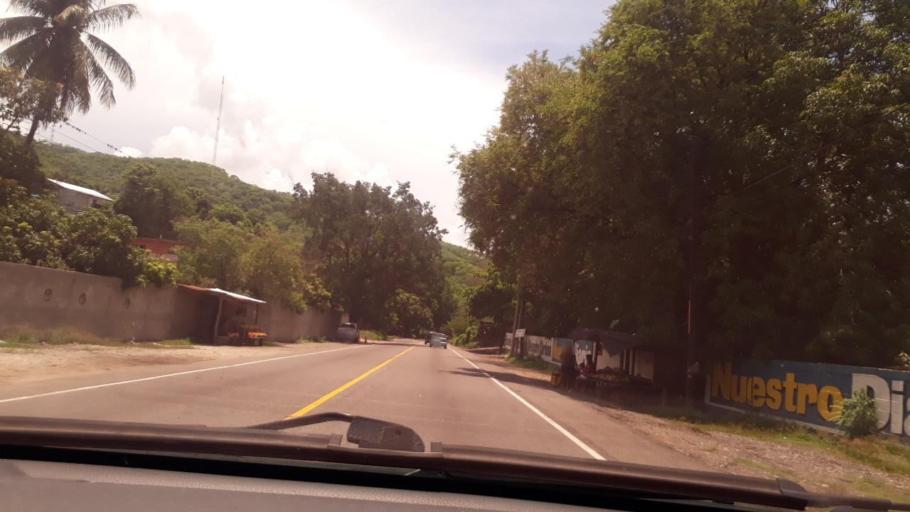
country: GT
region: Zacapa
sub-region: Municipio de Zacapa
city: Gualan
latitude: 15.1167
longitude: -89.4023
